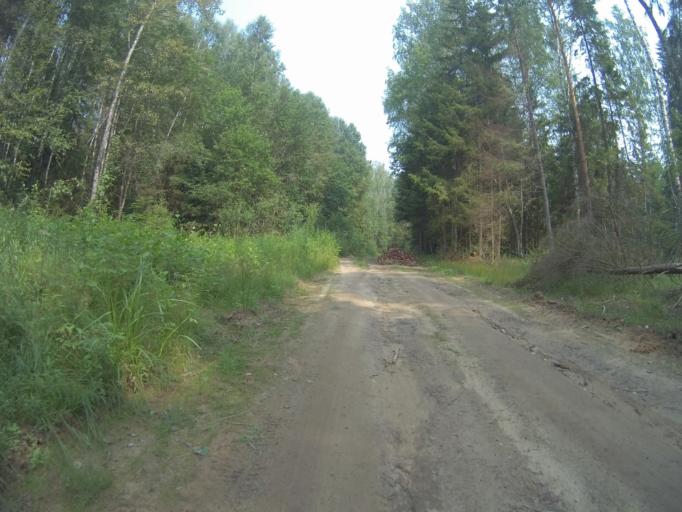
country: RU
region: Vladimir
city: Vorsha
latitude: 55.9778
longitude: 40.1877
